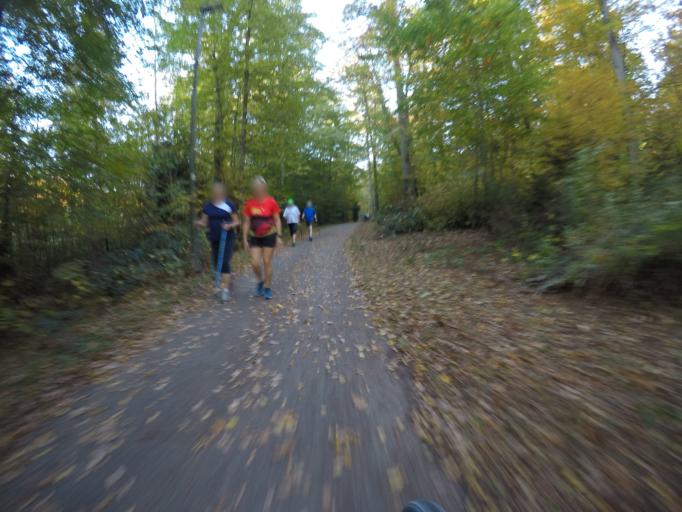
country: DE
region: Baden-Wuerttemberg
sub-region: Regierungsbezirk Stuttgart
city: Sindelfingen
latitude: 48.6944
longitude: 9.0337
